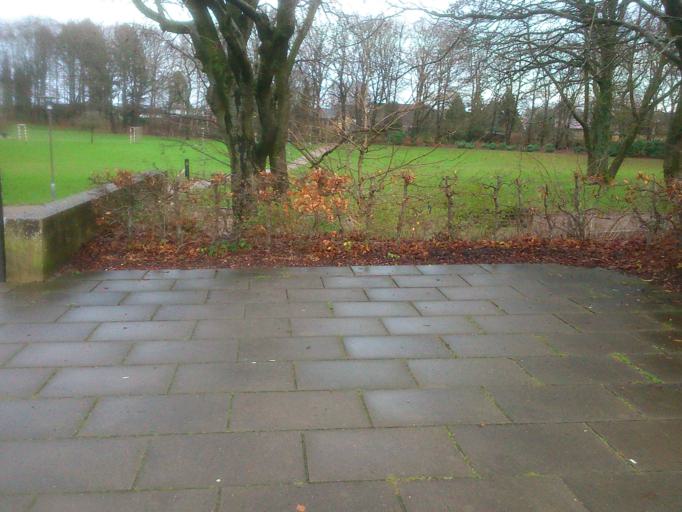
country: DK
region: Central Jutland
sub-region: Ikast-Brande Kommune
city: Ikast
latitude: 56.1421
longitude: 9.1641
